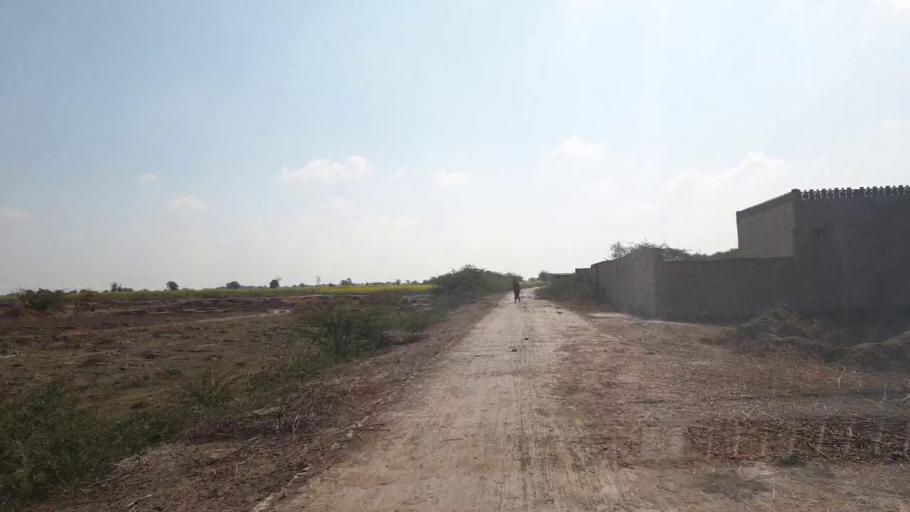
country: PK
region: Sindh
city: Shahpur Chakar
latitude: 26.0469
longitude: 68.6070
